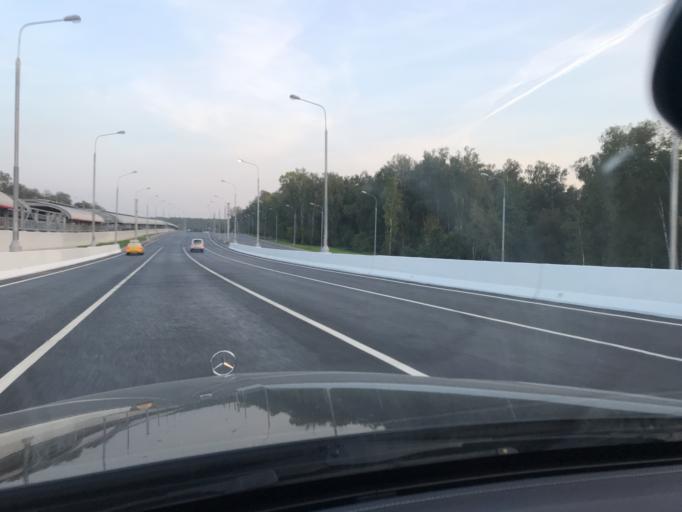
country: RU
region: Moscow
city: Solntsevo
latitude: 55.5965
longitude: 37.4153
